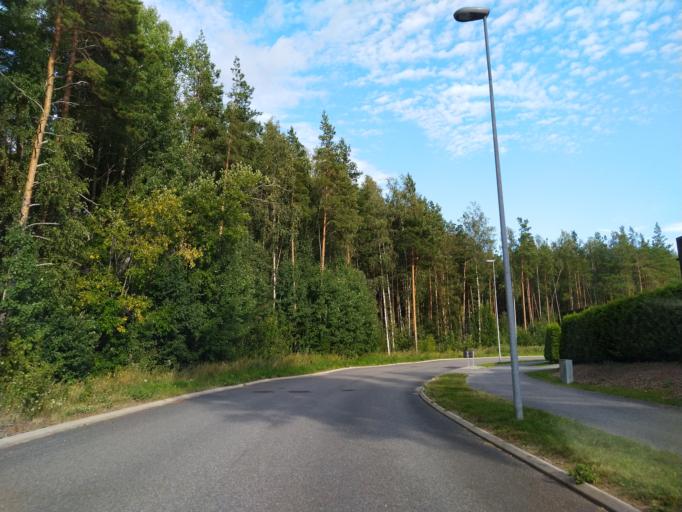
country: FI
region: Varsinais-Suomi
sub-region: Turku
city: Turku
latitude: 60.4239
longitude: 22.2124
